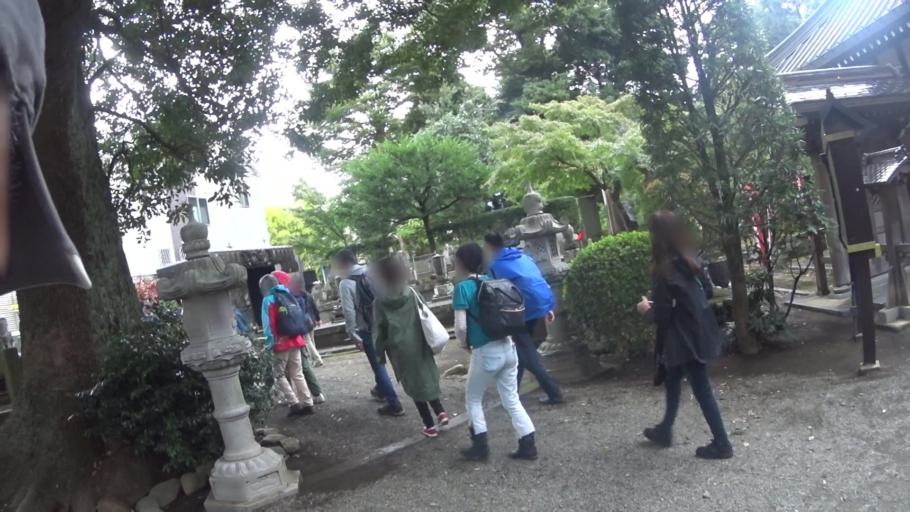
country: JP
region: Kanagawa
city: Hadano
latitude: 35.3707
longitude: 139.2138
